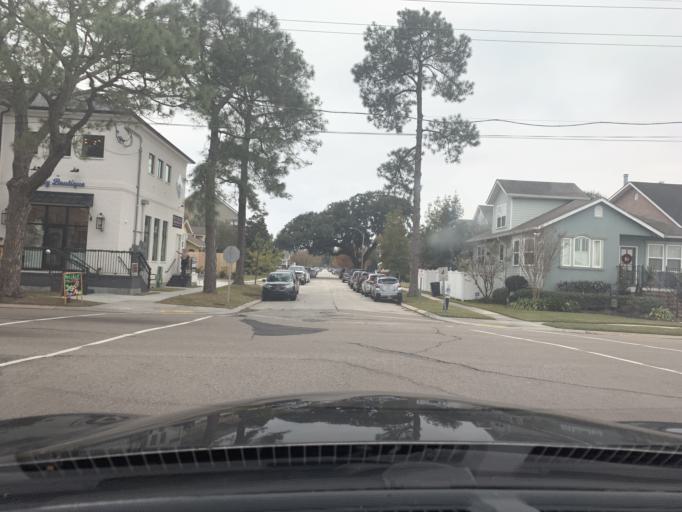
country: US
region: Louisiana
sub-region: Jefferson Parish
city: Metairie
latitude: 30.0050
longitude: -90.1114
